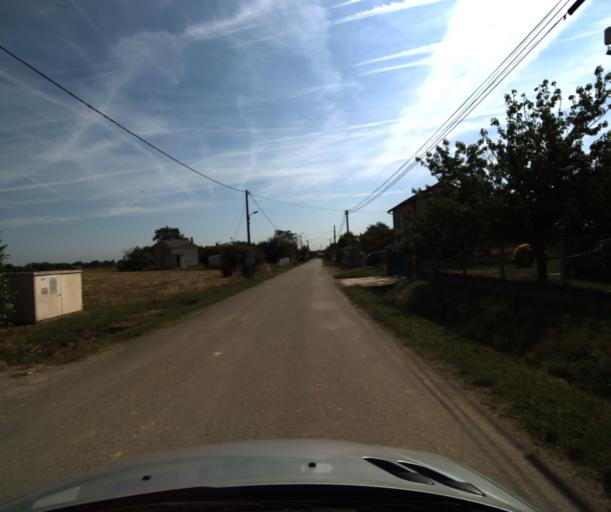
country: FR
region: Midi-Pyrenees
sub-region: Departement de la Haute-Garonne
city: Lherm
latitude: 43.4628
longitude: 1.2048
